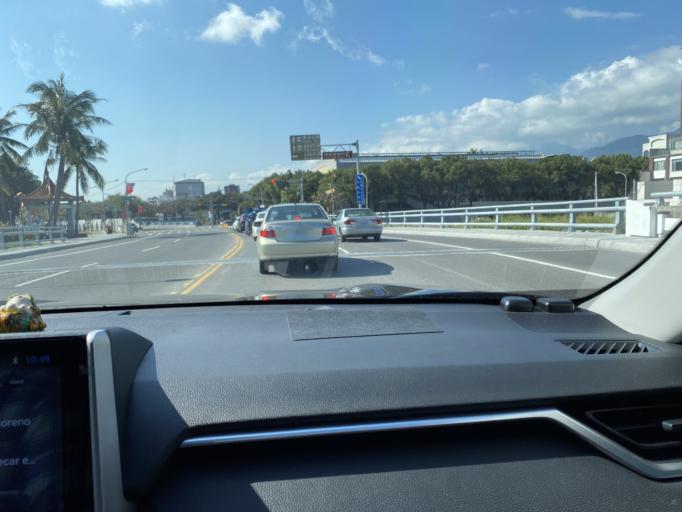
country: TW
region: Taiwan
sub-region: Hualien
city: Hualian
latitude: 23.9796
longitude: 121.6178
